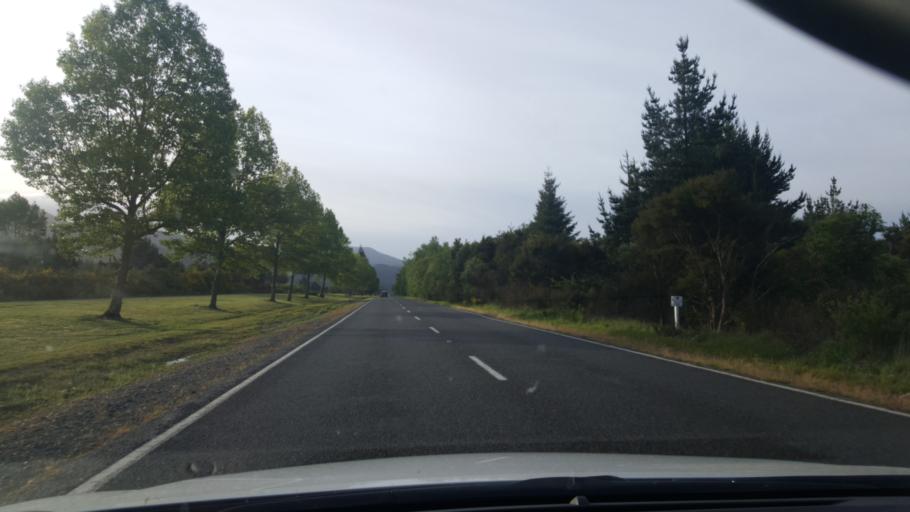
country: NZ
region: Waikato
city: Turangi
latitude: -38.9937
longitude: 175.7989
